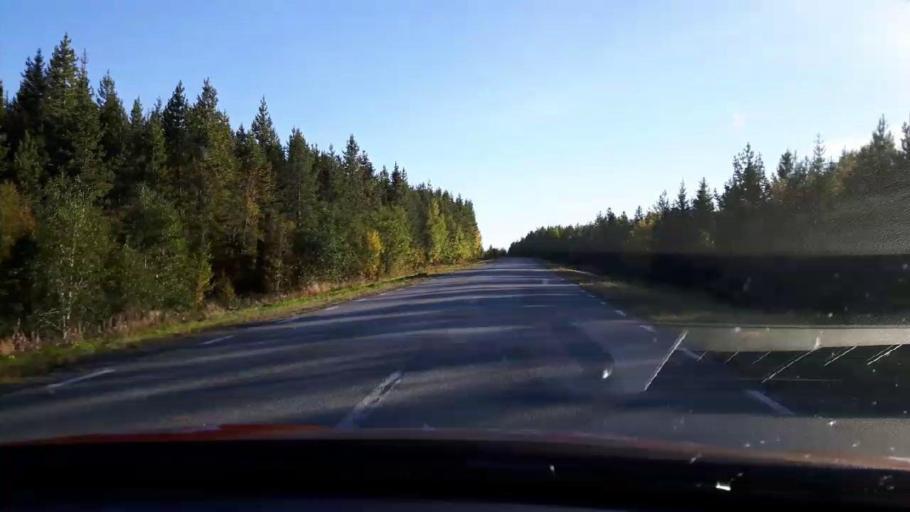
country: SE
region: Jaemtland
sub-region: OEstersunds Kommun
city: Lit
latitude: 63.7603
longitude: 14.7193
